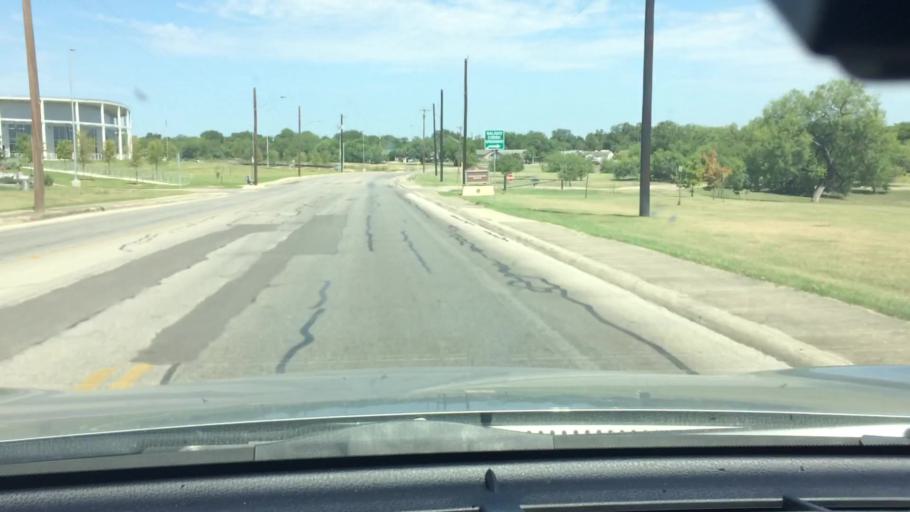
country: US
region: Texas
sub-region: Bexar County
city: San Antonio
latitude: 29.3880
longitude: -98.4316
